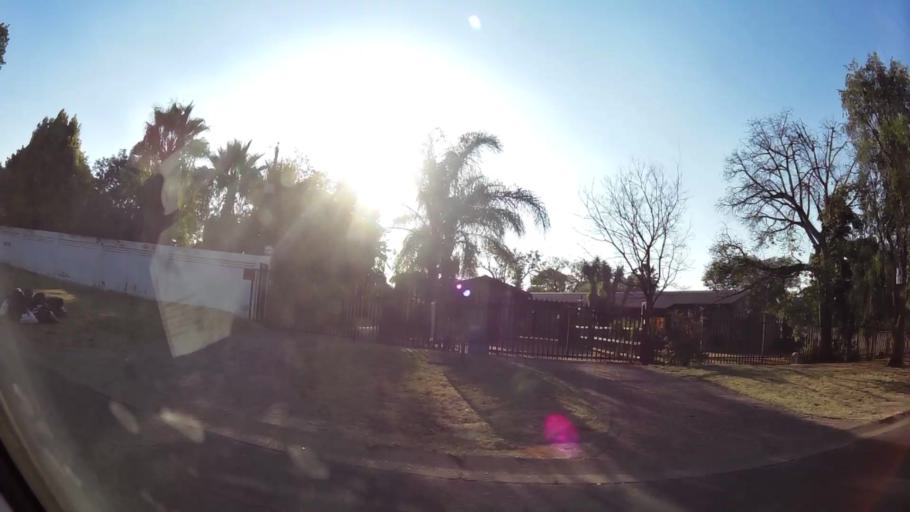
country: ZA
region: North-West
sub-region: Bojanala Platinum District Municipality
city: Rustenburg
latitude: -25.6814
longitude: 27.2288
